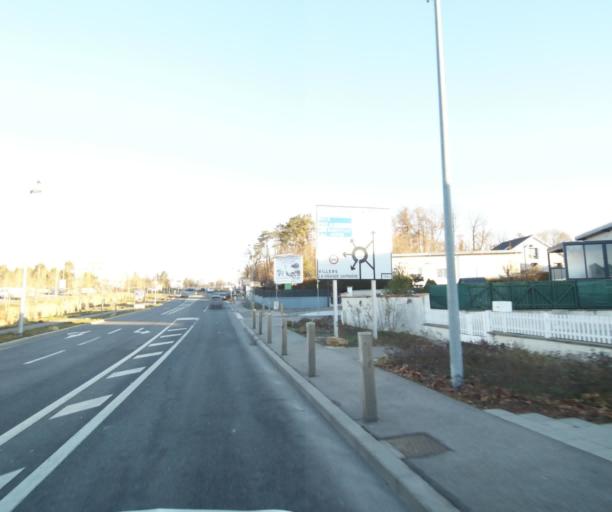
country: FR
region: Lorraine
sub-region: Departement de Meurthe-et-Moselle
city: Laxou
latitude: 48.6997
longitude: 6.1371
